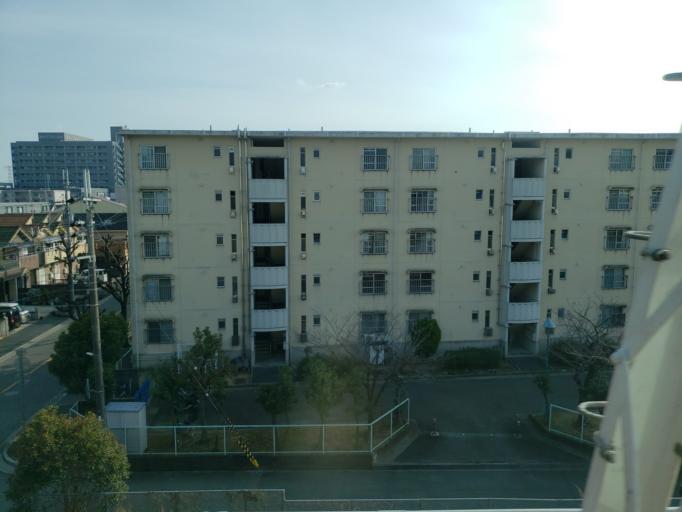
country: JP
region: Hyogo
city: Amagasaki
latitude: 34.7388
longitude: 135.3834
